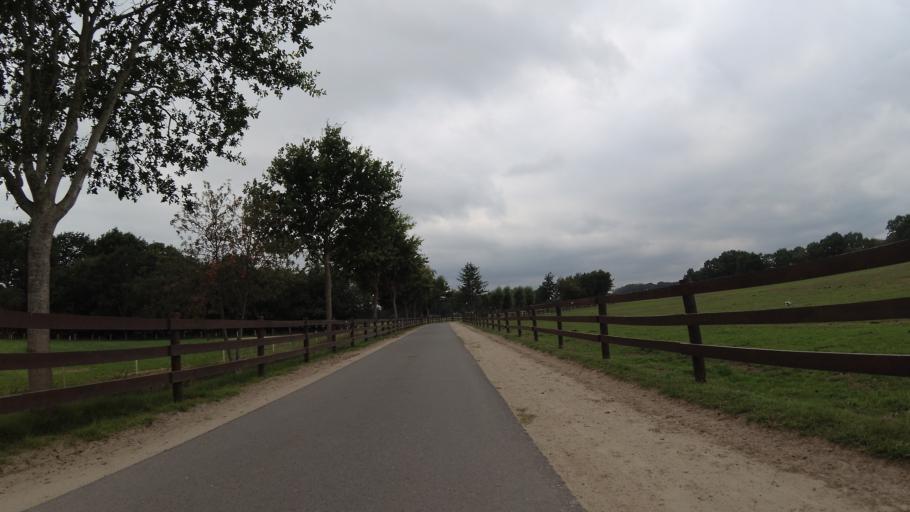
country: DE
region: Lower Saxony
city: Oberlangen
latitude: 52.8333
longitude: 7.2669
